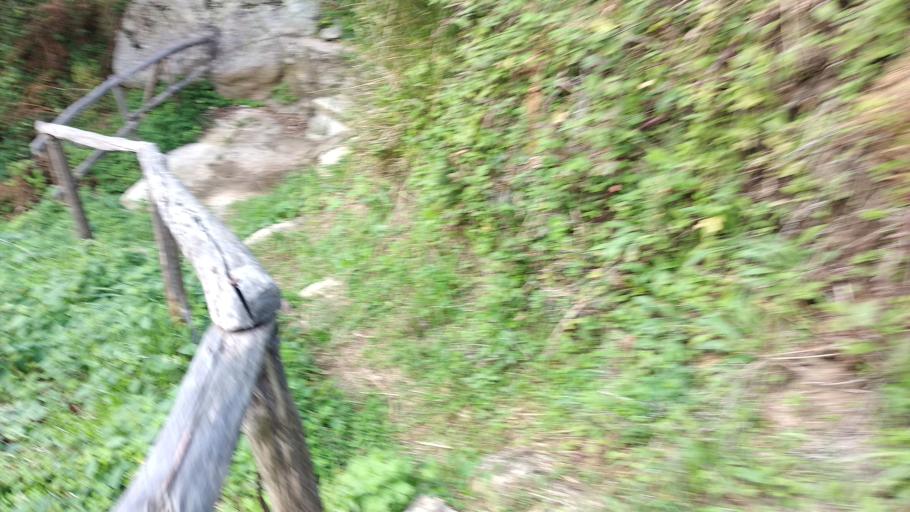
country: IT
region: Calabria
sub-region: Provincia di Reggio Calabria
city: San Roberto
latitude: 38.2381
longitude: 15.7756
